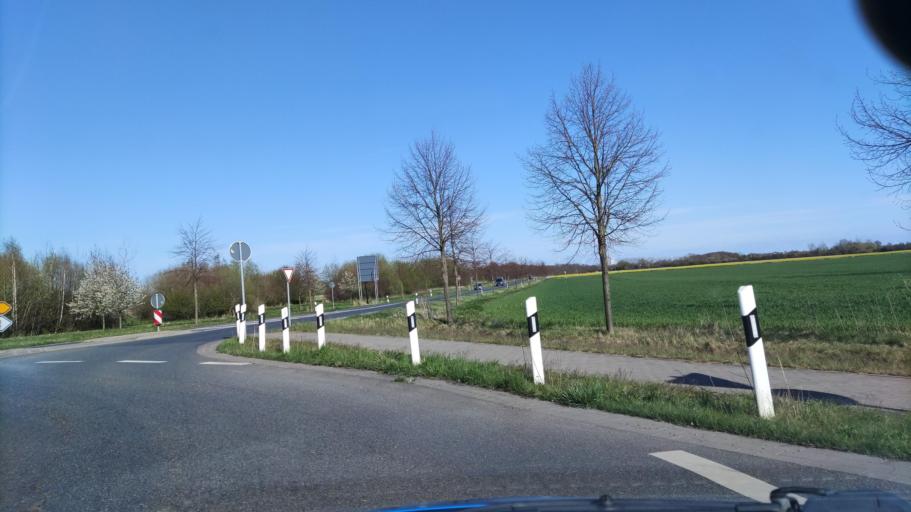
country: DE
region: Lower Saxony
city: Sehnde
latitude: 52.3313
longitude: 9.9691
